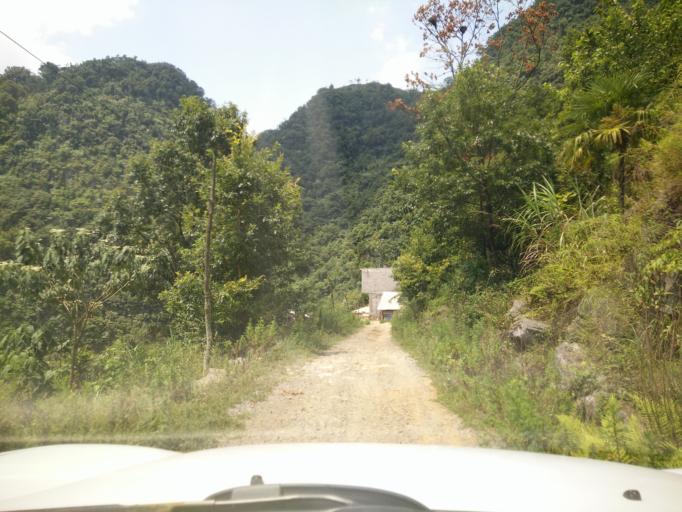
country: CN
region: Guangxi Zhuangzu Zizhiqu
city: Xinzhou
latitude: 25.0156
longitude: 105.7043
